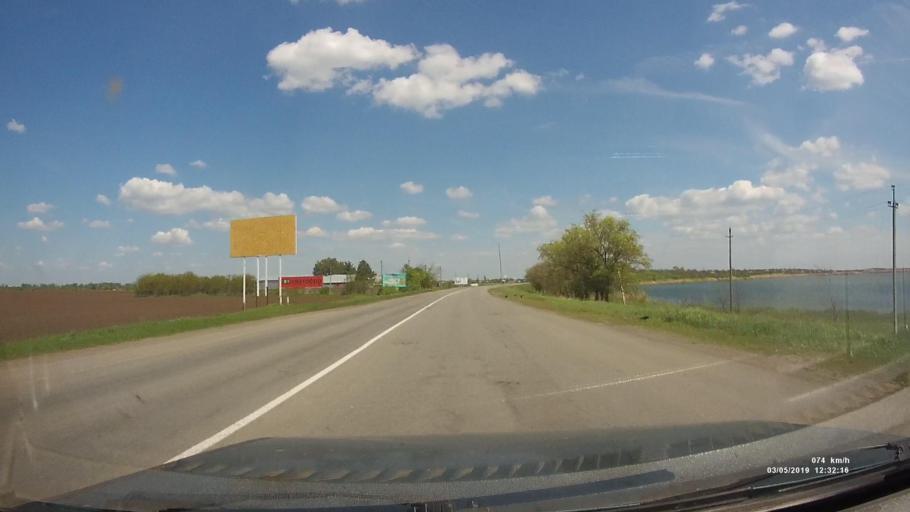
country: RU
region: Rostov
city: Semikarakorsk
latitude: 47.5104
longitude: 40.7566
